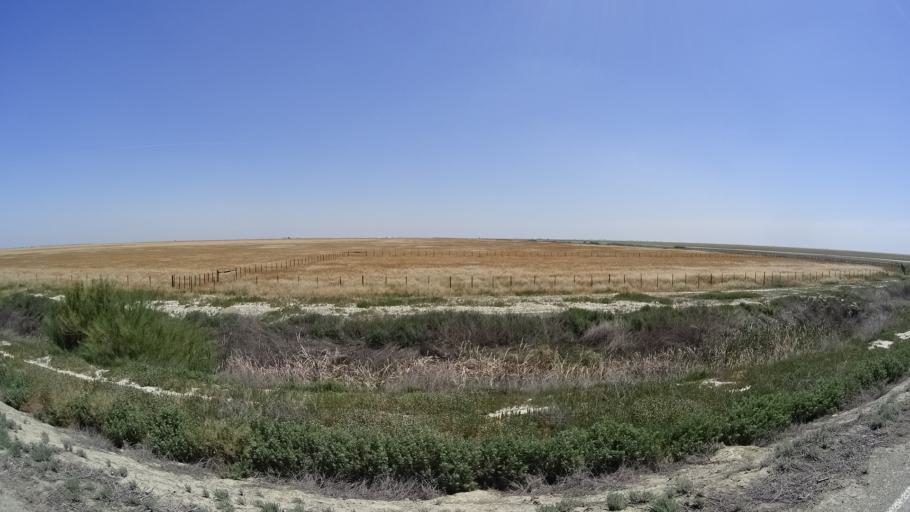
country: US
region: California
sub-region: Tulare County
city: Alpaugh
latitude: 35.9355
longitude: -119.6447
